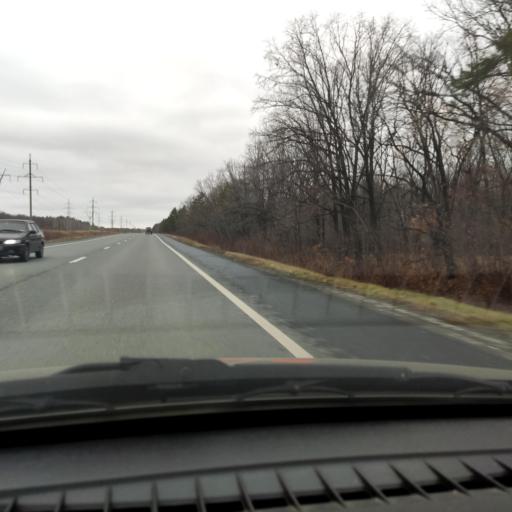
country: RU
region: Samara
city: Bogatyr'
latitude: 53.5018
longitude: 49.9491
